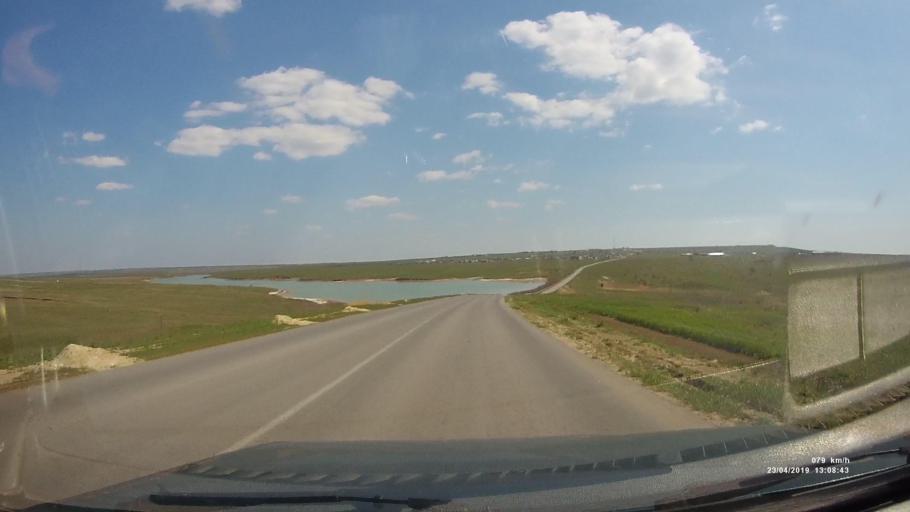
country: RU
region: Kalmykiya
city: Yashalta
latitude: 46.5808
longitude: 42.7791
